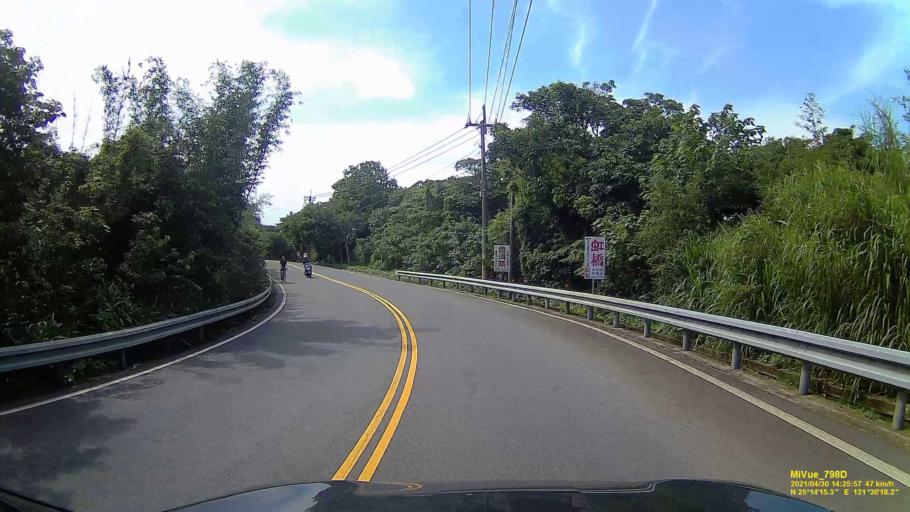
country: TW
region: Taipei
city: Taipei
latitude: 25.2378
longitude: 121.5048
